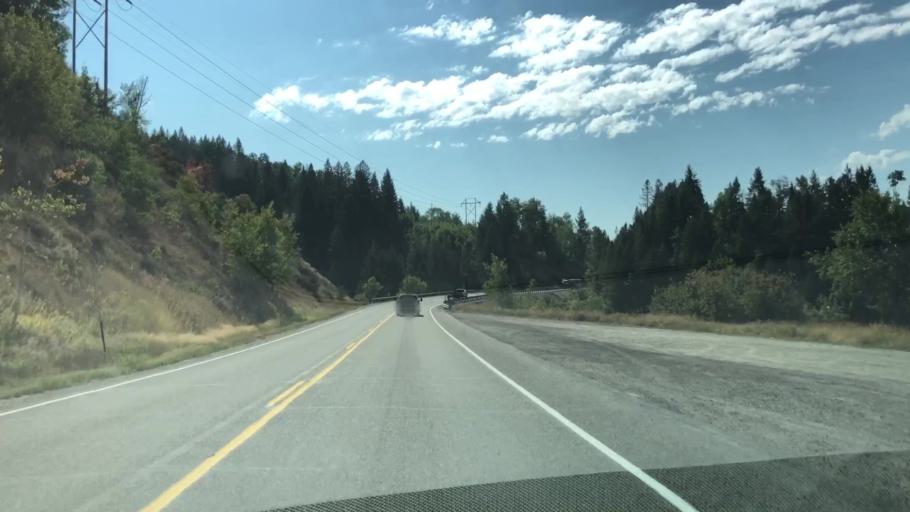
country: US
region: Idaho
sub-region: Teton County
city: Victor
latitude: 43.3008
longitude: -111.1307
